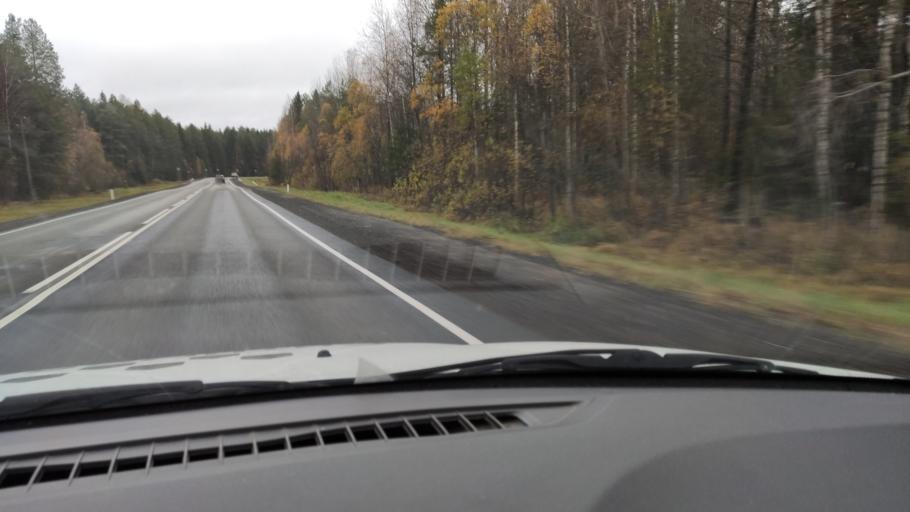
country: RU
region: Kirov
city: Belaya Kholunitsa
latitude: 58.8803
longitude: 50.8715
